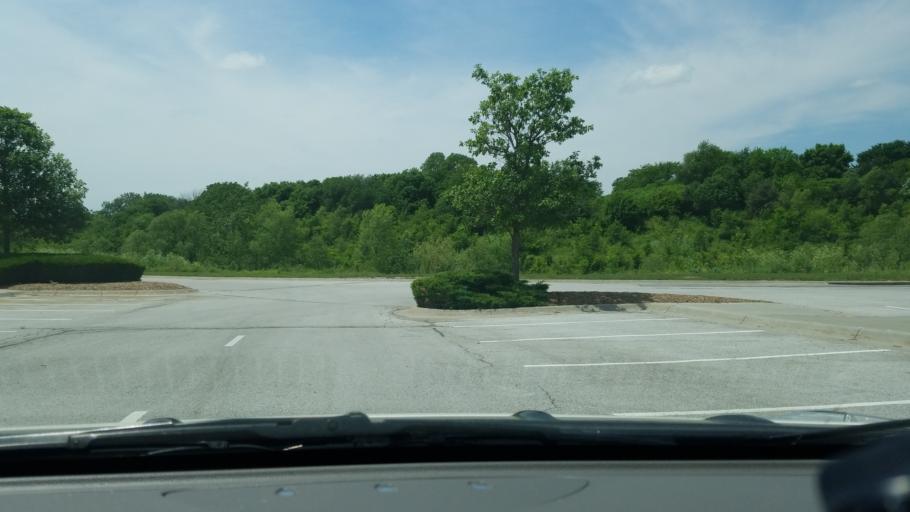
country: US
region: Nebraska
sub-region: Sarpy County
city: Papillion
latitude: 41.1342
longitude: -96.0316
